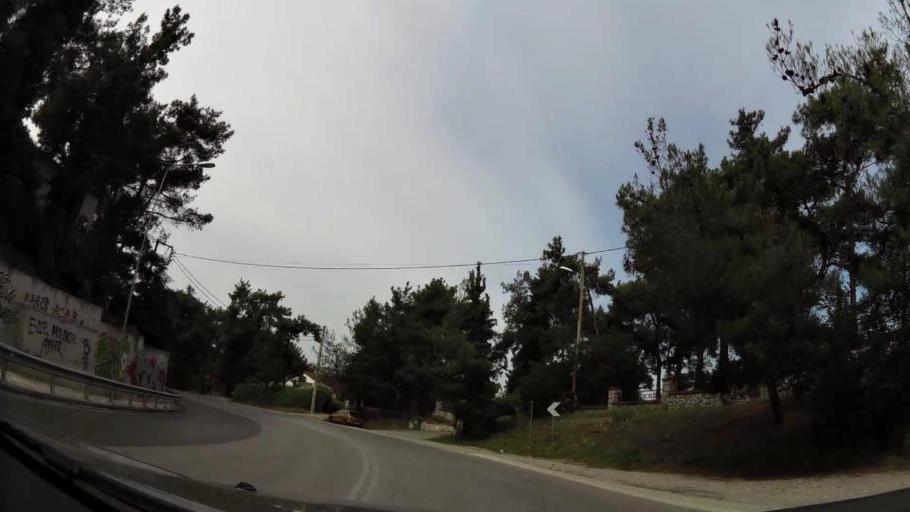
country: GR
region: Central Macedonia
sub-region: Nomos Thessalonikis
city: Panorama
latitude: 40.5929
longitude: 23.0158
